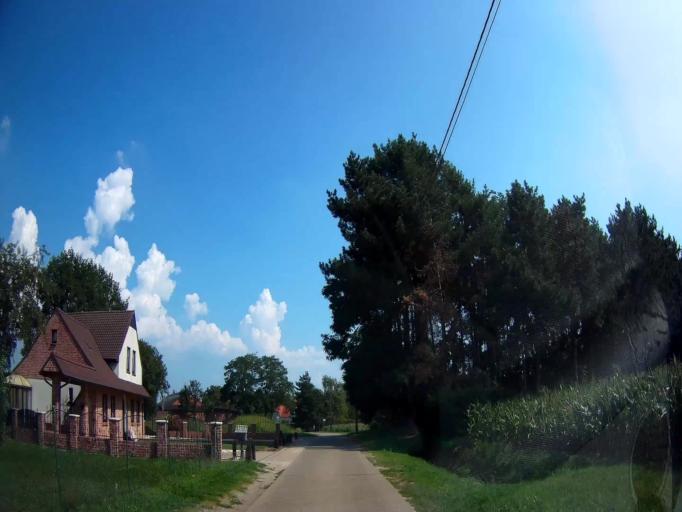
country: BE
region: Flanders
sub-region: Provincie Antwerpen
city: Retie
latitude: 51.2721
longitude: 5.0362
